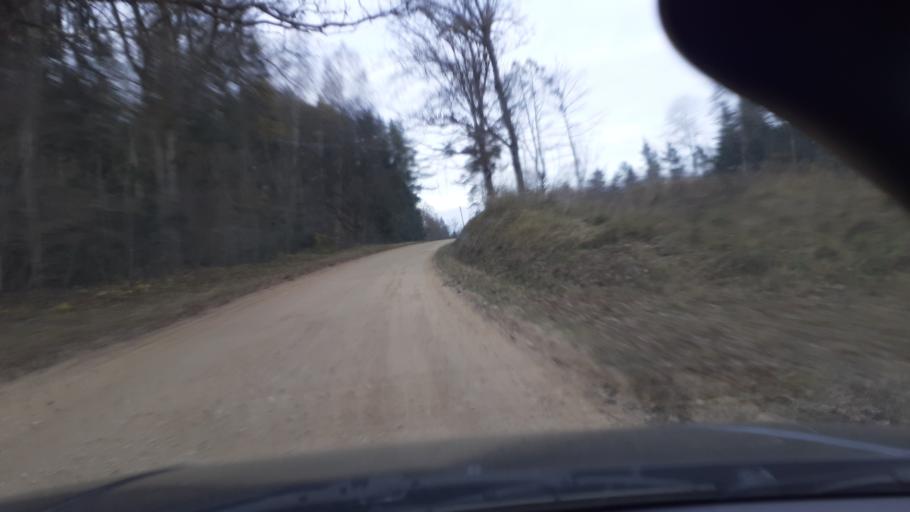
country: LV
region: Alsunga
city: Alsunga
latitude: 56.9706
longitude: 21.6635
